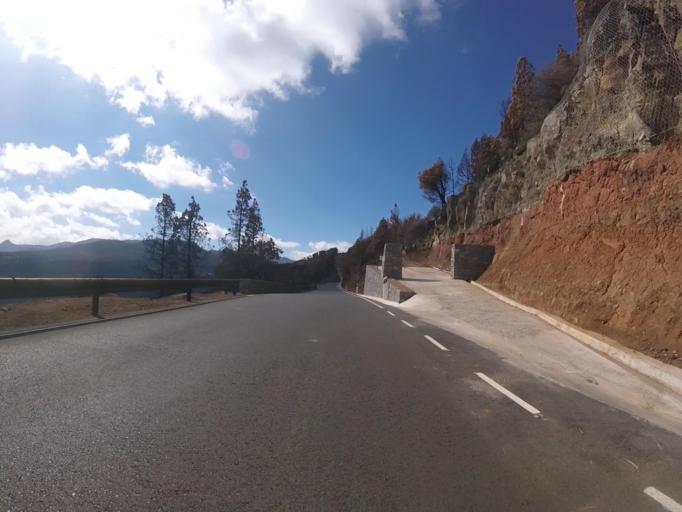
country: ES
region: Canary Islands
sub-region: Provincia de Las Palmas
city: Tejeda
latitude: 27.9988
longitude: -15.5953
